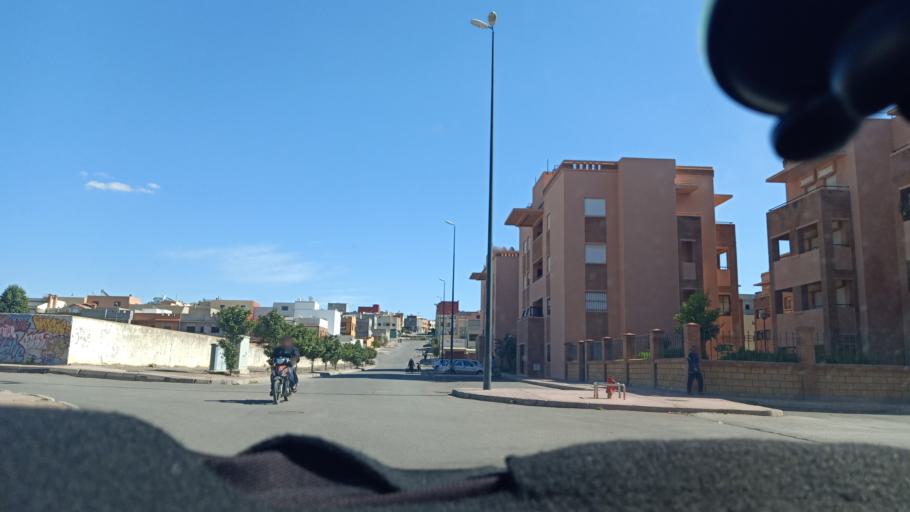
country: MA
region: Doukkala-Abda
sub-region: Safi
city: Youssoufia
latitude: 32.2414
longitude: -8.5342
